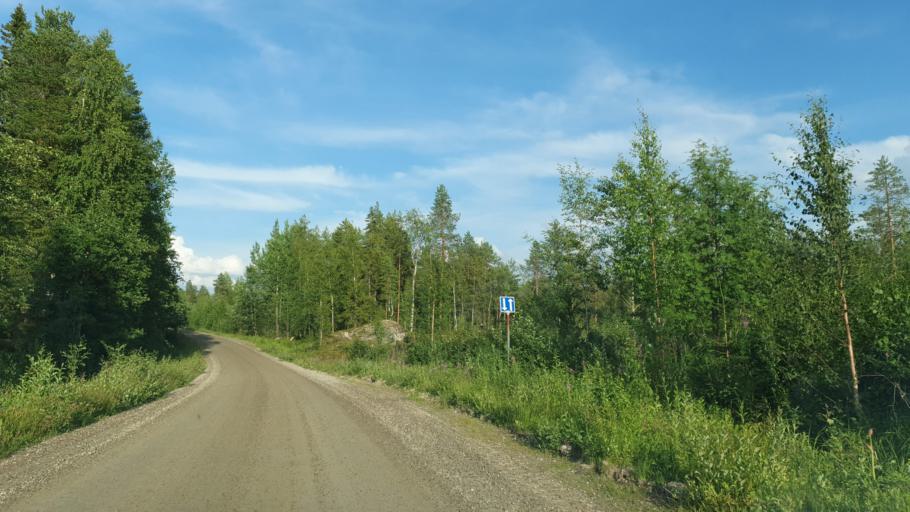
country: FI
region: Kainuu
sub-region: Kehys-Kainuu
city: Kuhmo
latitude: 64.2670
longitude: 29.8122
